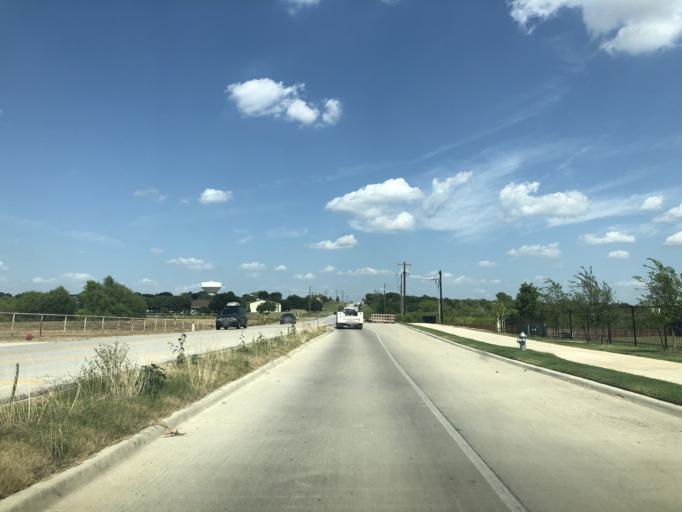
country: US
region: Texas
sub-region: Tarrant County
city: Haslet
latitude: 32.9241
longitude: -97.3406
